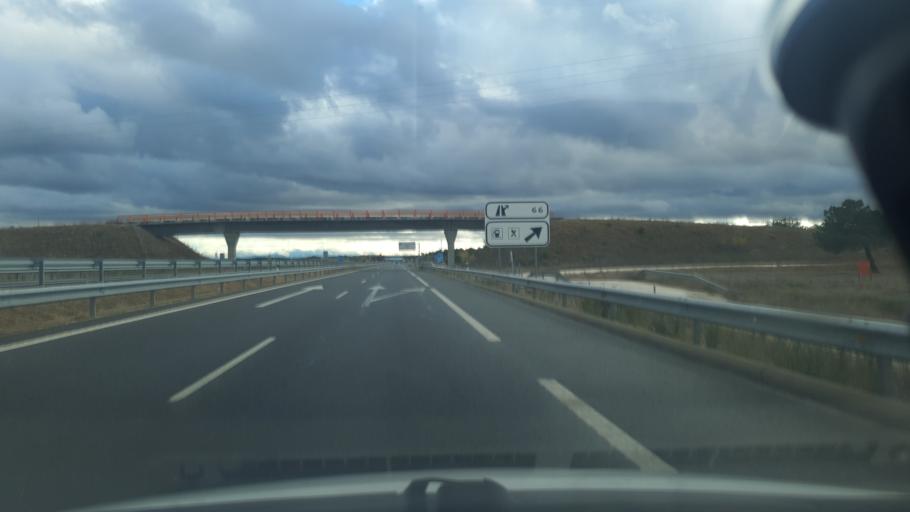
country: ES
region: Castille and Leon
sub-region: Provincia de Segovia
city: Sanchonuno
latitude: 41.3022
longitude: -4.3019
